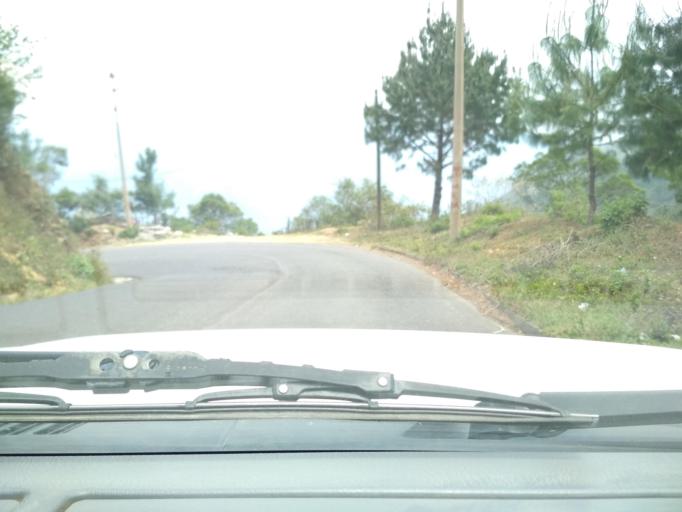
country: MX
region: Veracruz
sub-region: Camerino Z. Mendoza
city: La Cuesta
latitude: 18.7861
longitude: -97.1609
